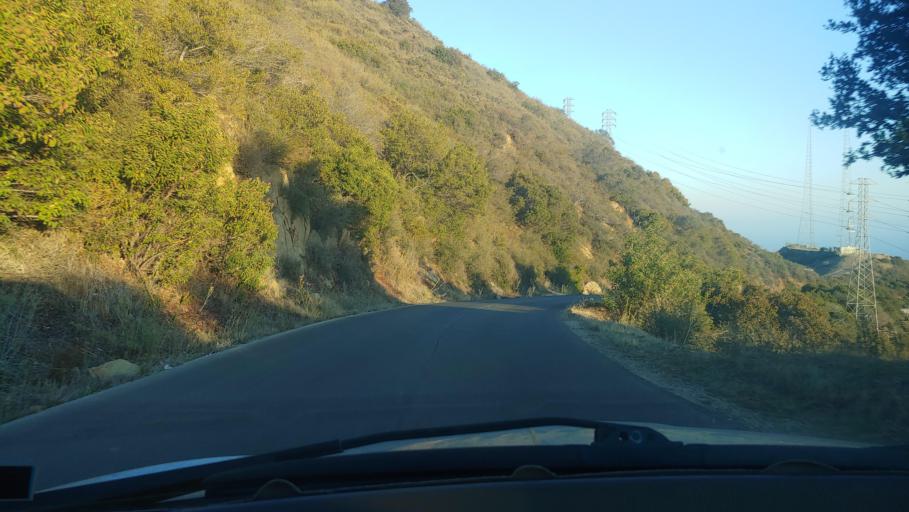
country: US
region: California
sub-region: Santa Barbara County
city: Mission Canyon
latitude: 34.4734
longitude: -119.6807
